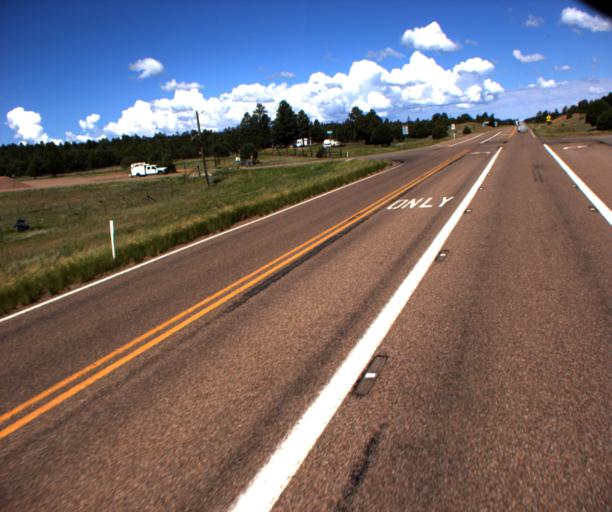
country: US
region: Arizona
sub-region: Navajo County
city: Linden
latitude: 34.3177
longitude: -110.2470
